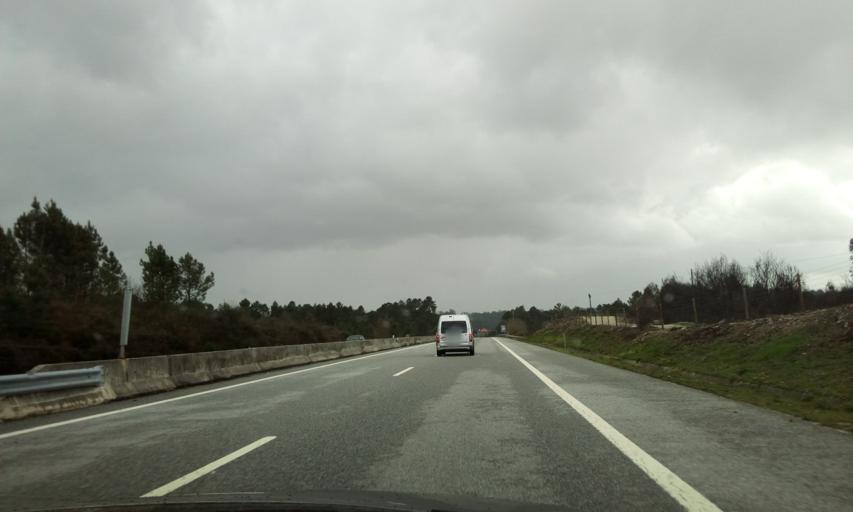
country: PT
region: Viseu
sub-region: Viseu
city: Rio de Loba
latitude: 40.6398
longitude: -7.8763
